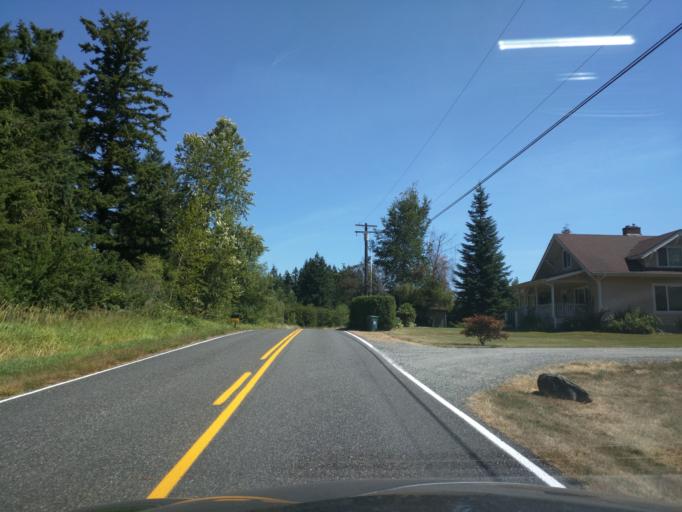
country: US
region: Washington
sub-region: Whatcom County
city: Geneva
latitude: 48.7993
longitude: -122.4223
